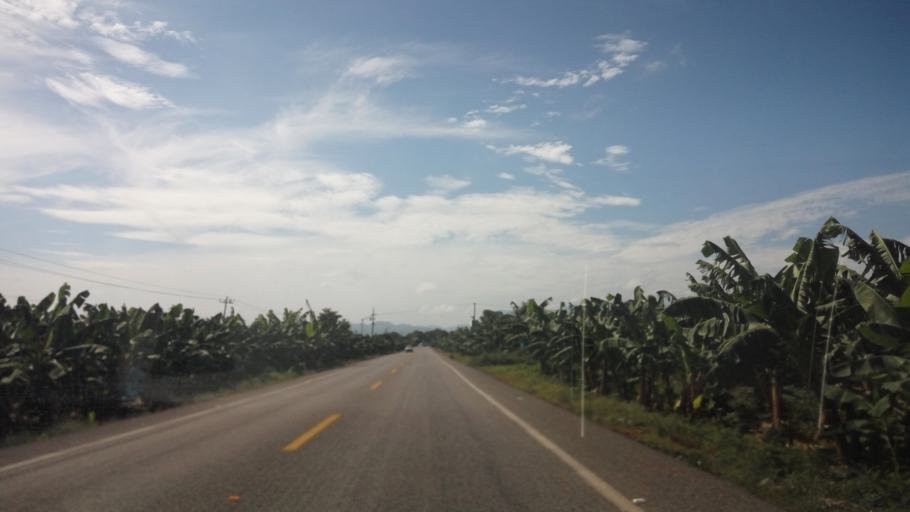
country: MX
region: Tabasco
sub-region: Teapa
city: Eureka y Belen
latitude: 17.6351
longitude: -92.9665
